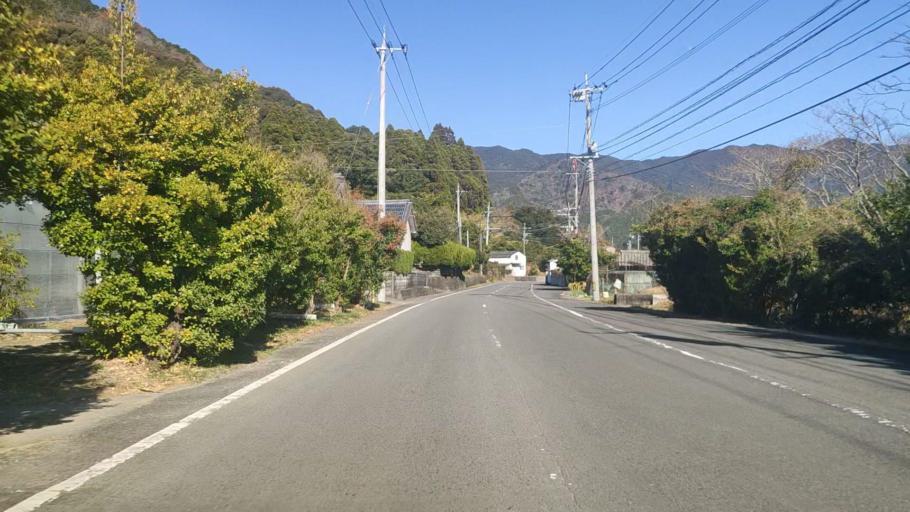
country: JP
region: Oita
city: Saiki
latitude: 32.8019
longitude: 131.8881
